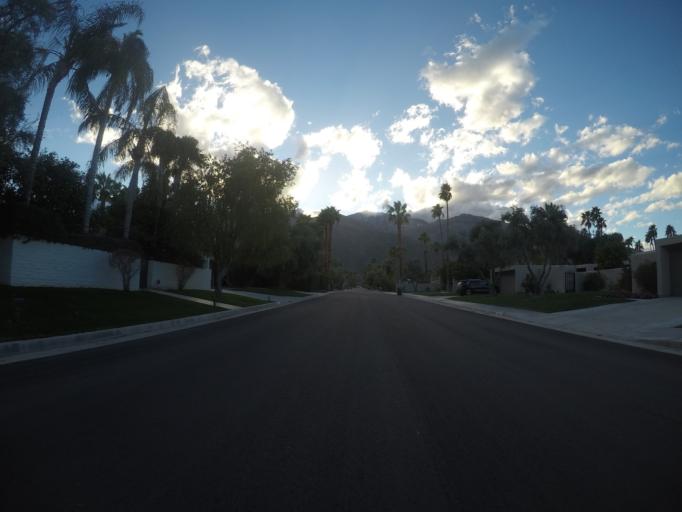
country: US
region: California
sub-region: Riverside County
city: Palm Springs
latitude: 33.7981
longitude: -116.5341
